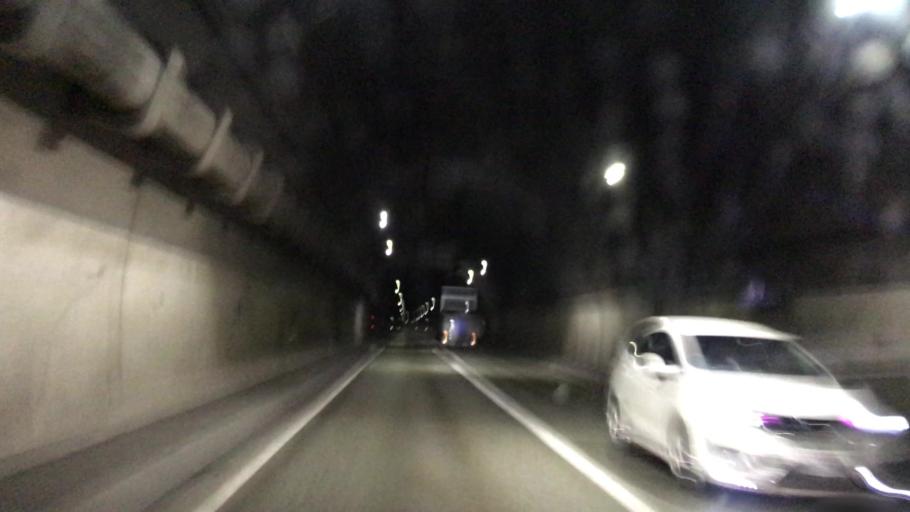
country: JP
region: Hokkaido
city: Shimo-furano
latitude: 42.9029
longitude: 142.3201
